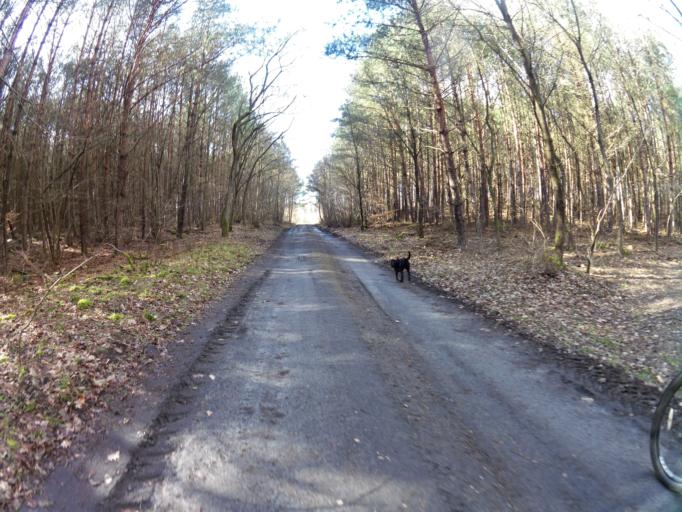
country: PL
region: West Pomeranian Voivodeship
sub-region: Powiat mysliborski
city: Debno
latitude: 52.7547
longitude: 14.7203
